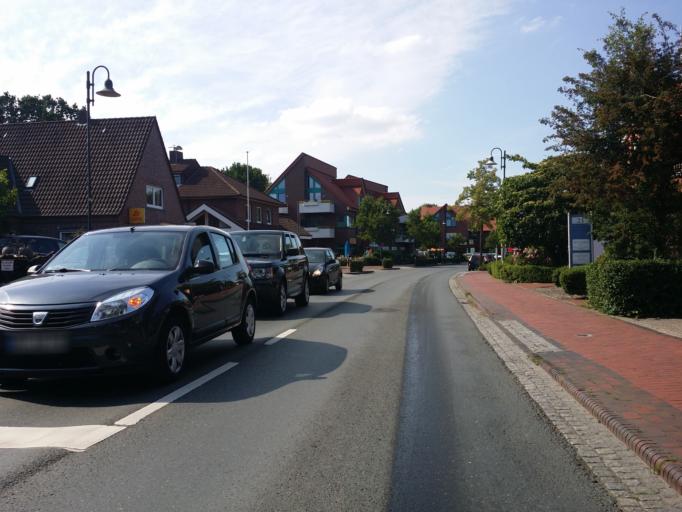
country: DE
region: Lower Saxony
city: Wiefelstede
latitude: 53.2567
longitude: 8.1160
